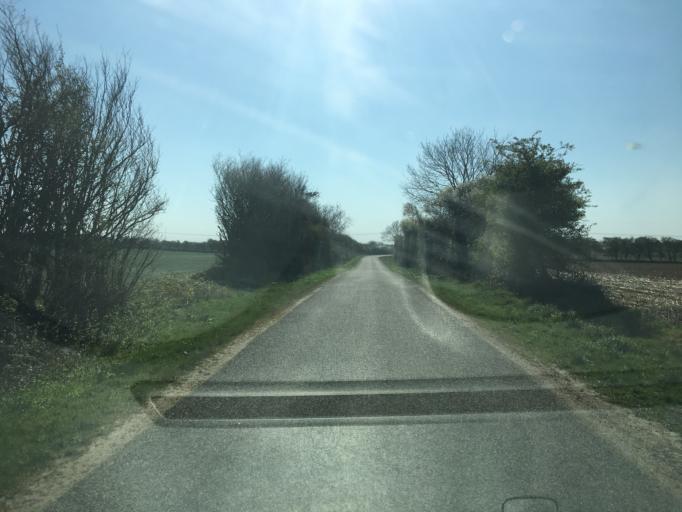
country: DK
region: South Denmark
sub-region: Aabenraa Kommune
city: Rodekro
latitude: 54.9948
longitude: 9.3095
